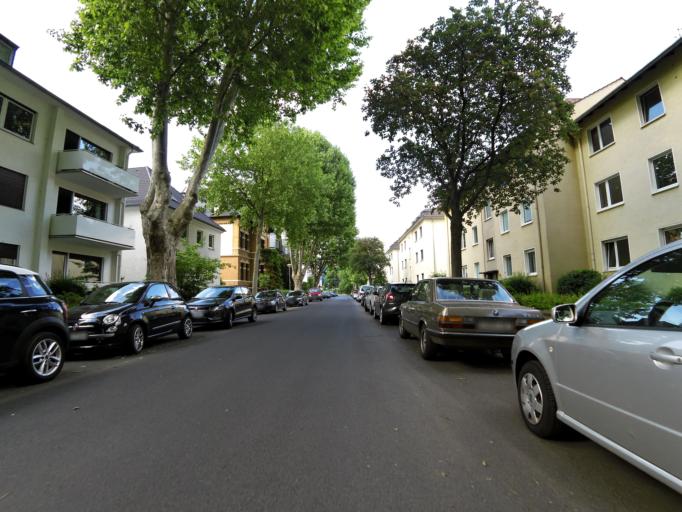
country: DE
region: Rheinland-Pfalz
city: Koblenz
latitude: 50.3511
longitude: 7.5988
